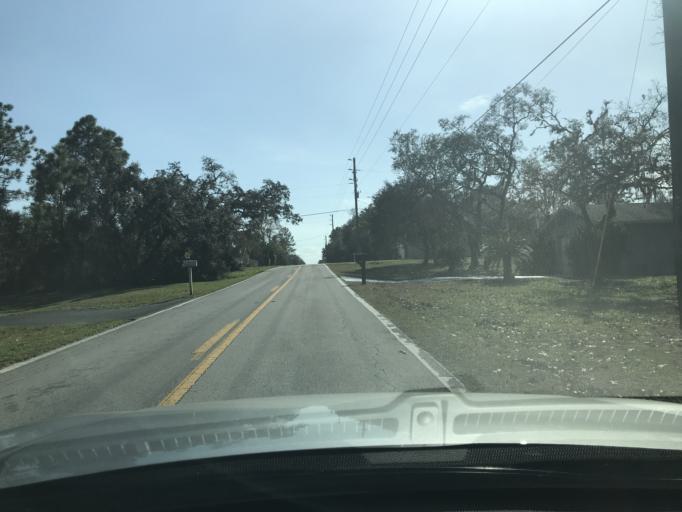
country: US
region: Florida
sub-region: Hernando County
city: North Weeki Wachee
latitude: 28.5517
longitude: -82.5477
